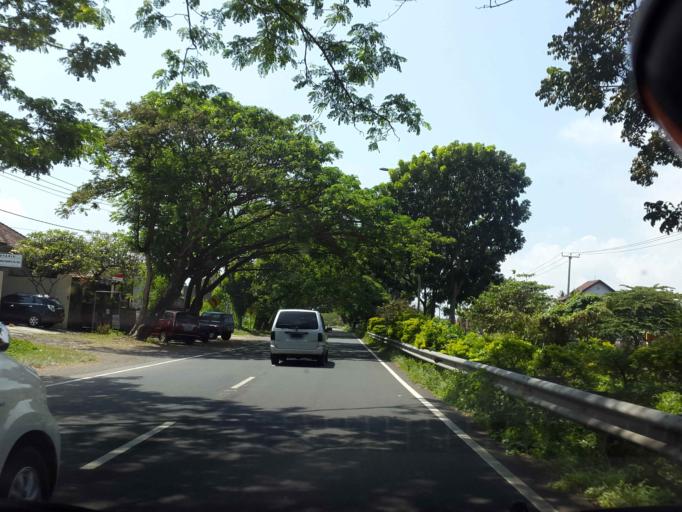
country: ID
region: Bali
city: Semarapura
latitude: -8.5682
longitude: 115.3819
